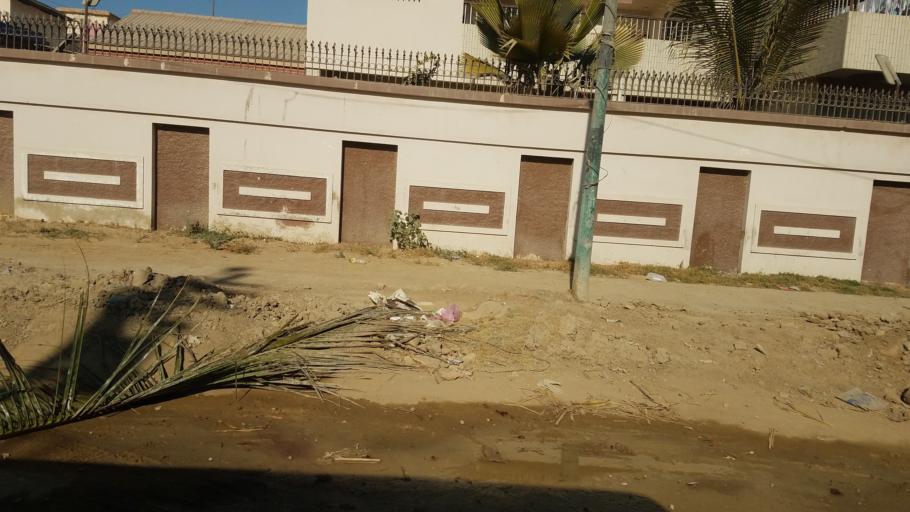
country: PK
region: Sindh
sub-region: Karachi District
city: Karachi
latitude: 24.9232
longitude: 67.0490
